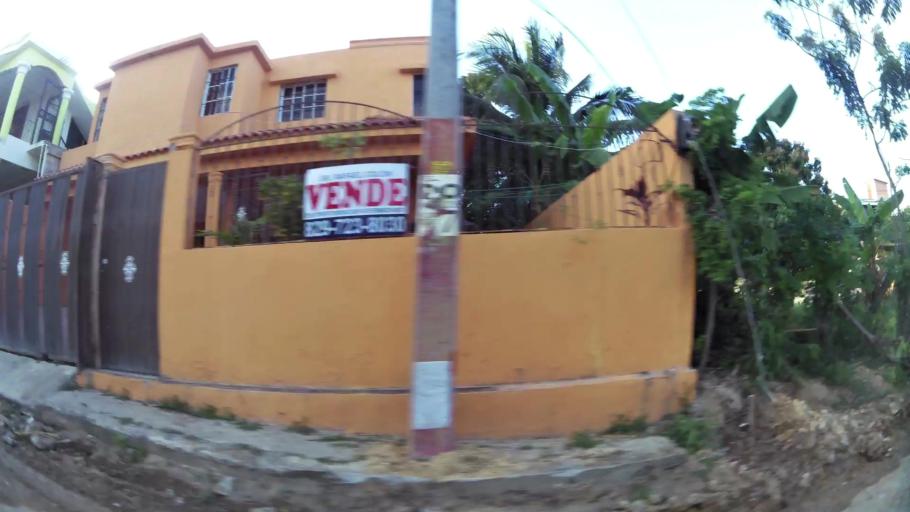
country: DO
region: Nacional
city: La Agustina
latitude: 18.5500
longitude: -69.9211
